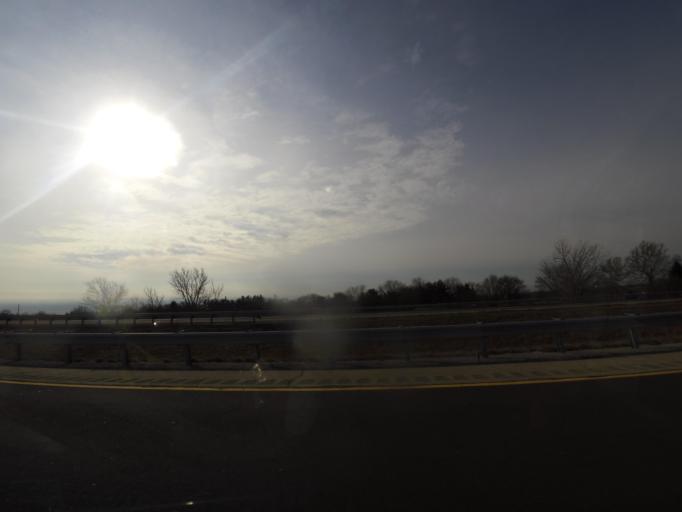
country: US
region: Illinois
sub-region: Macon County
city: Decatur
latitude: 39.7858
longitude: -88.9797
